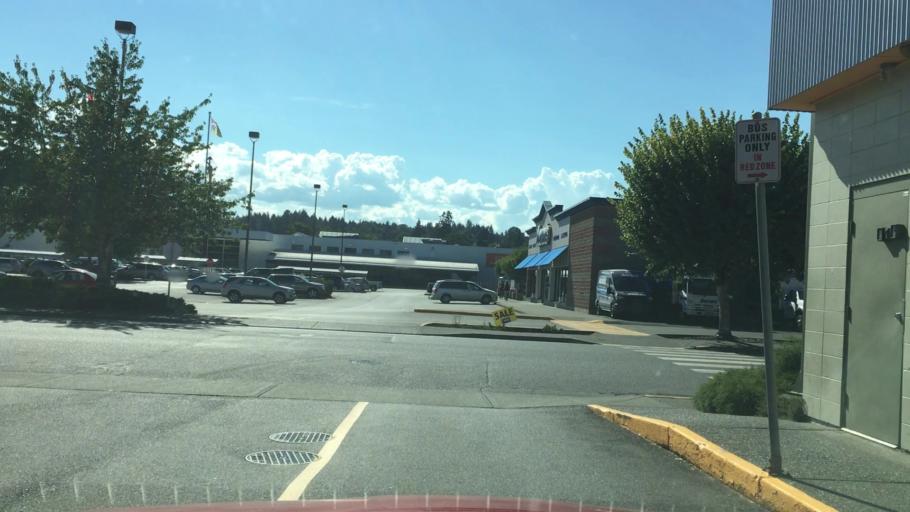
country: CA
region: British Columbia
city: Duncan
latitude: 48.7748
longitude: -123.7014
